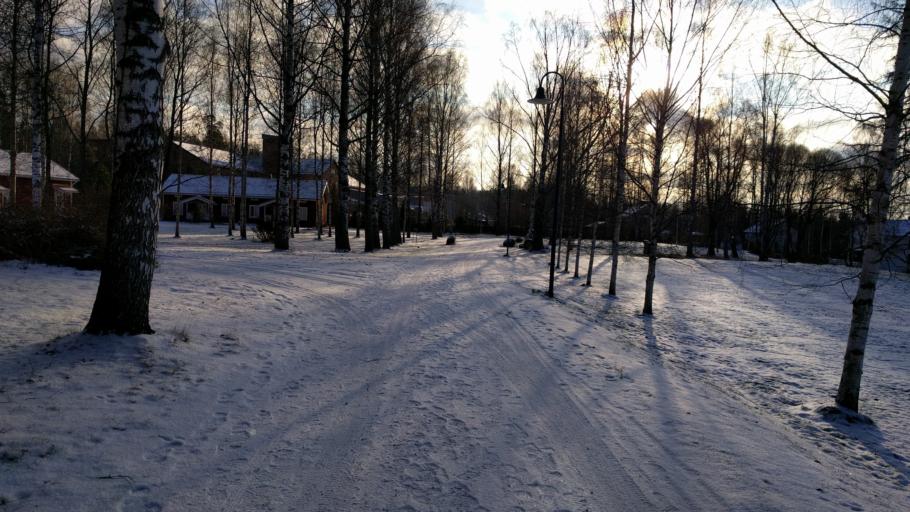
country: FI
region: Paijanne Tavastia
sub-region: Lahti
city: Heinola
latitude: 61.1678
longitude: 25.9866
